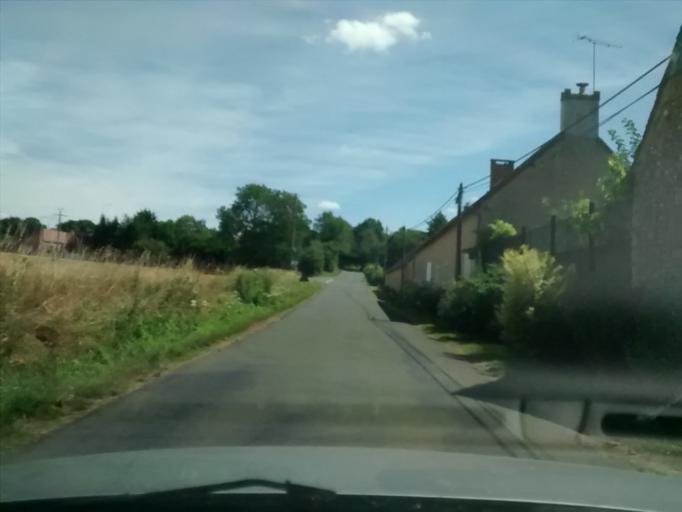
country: FR
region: Pays de la Loire
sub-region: Departement de la Sarthe
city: Loue
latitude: 48.0311
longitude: -0.1083
